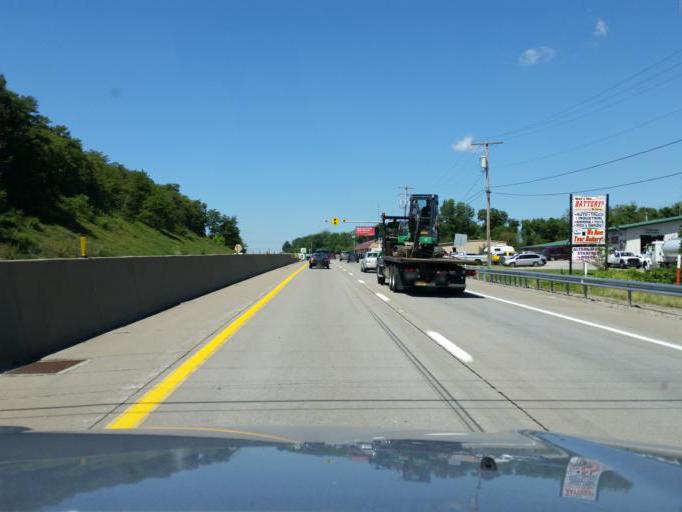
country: US
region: Pennsylvania
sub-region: Westmoreland County
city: Delmont
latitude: 40.4023
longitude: -79.5181
